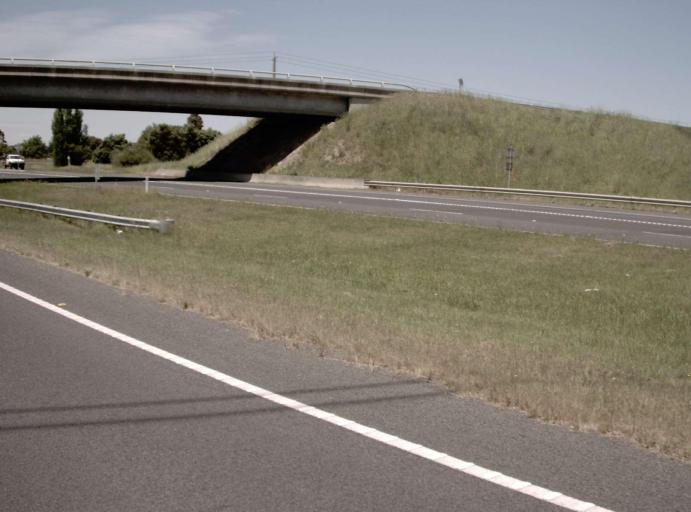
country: AU
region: Victoria
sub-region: Latrobe
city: Morwell
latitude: -38.2451
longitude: 146.4361
